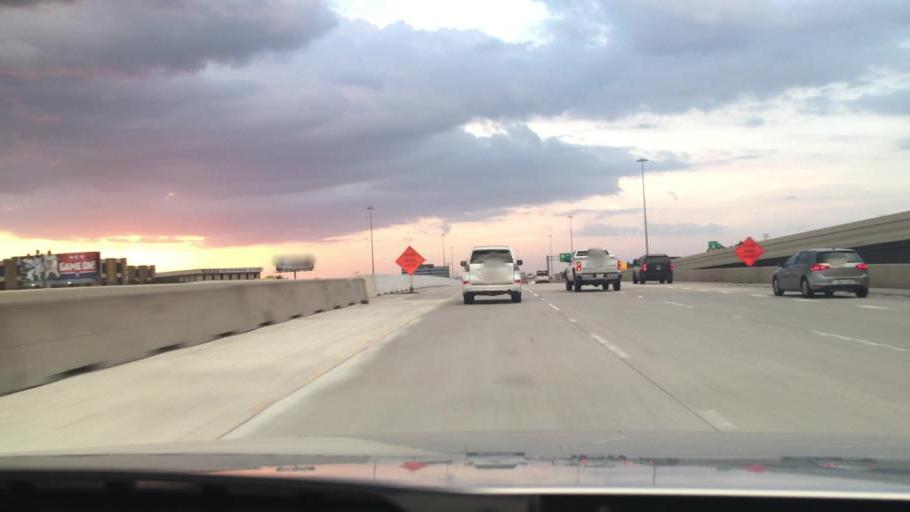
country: US
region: Texas
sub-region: Harris County
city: Spring Valley
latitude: 29.8071
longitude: -95.4550
